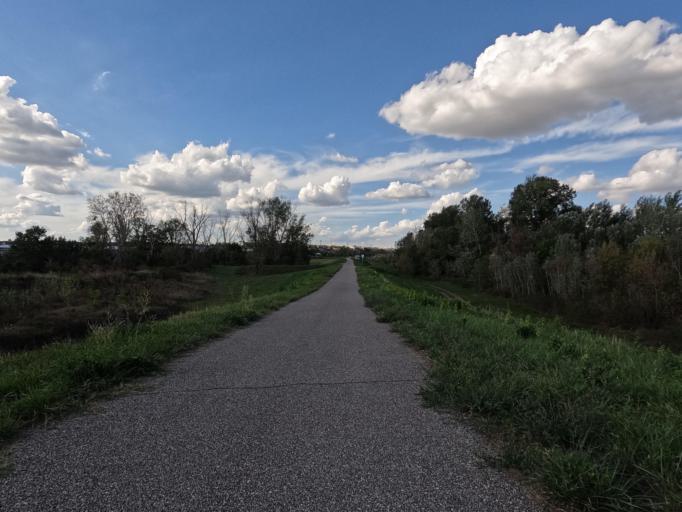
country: HU
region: Tolna
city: Paks
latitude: 46.5977
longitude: 18.8576
